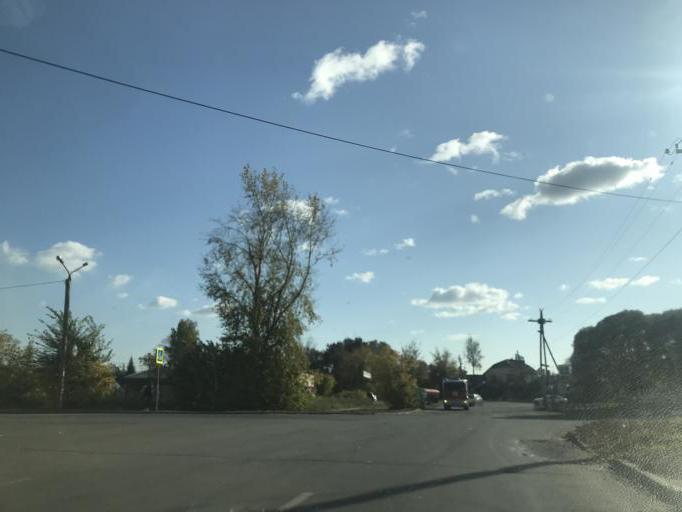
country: RU
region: Chelyabinsk
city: Dolgoderevenskoye
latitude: 55.2584
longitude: 61.3635
